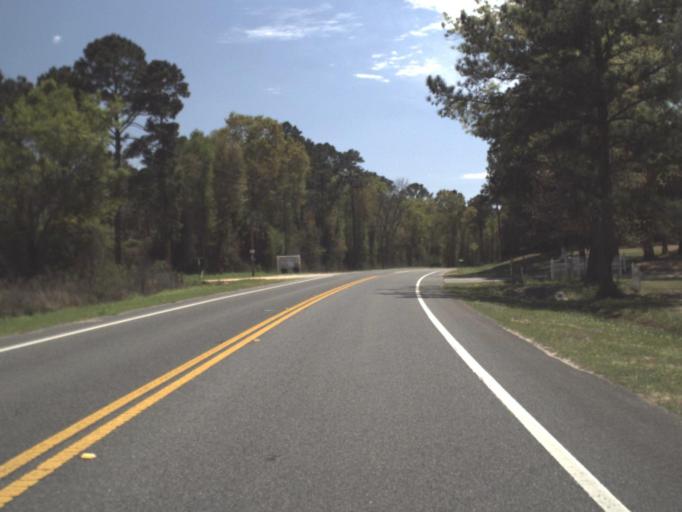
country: US
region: Alabama
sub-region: Geneva County
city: Geneva
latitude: 30.8627
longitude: -85.9441
